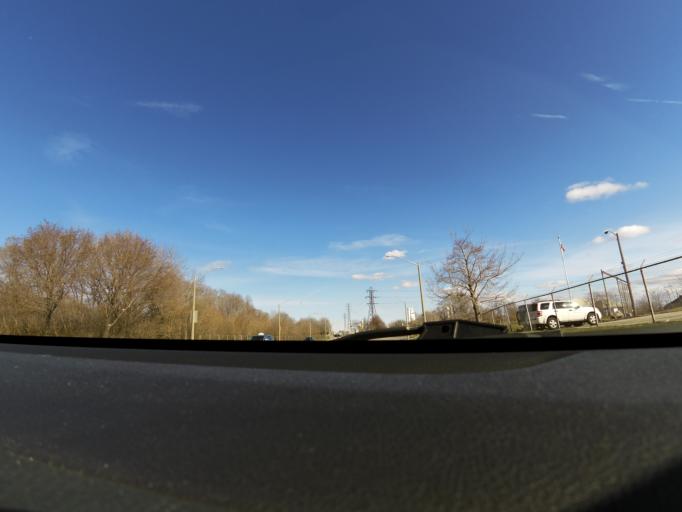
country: CA
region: Ontario
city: Hamilton
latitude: 43.2666
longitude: -79.8365
